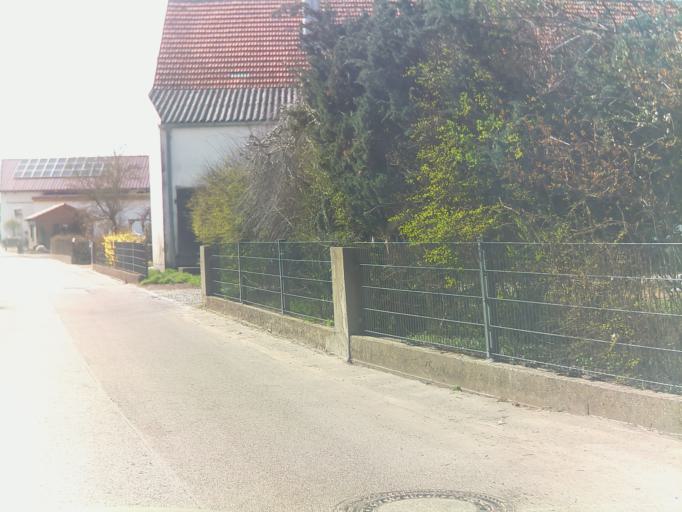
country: DE
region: Bavaria
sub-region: Swabia
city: Inchenhofen
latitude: 48.5482
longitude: 11.1224
